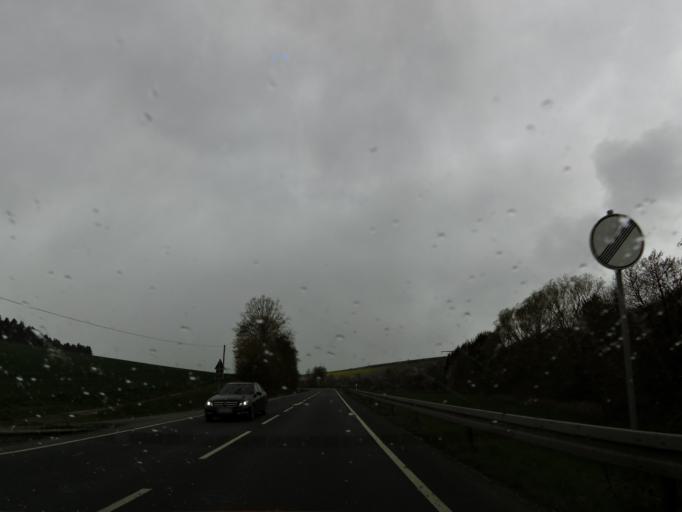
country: DE
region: Lower Saxony
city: Hahausen
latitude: 51.9475
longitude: 10.1737
